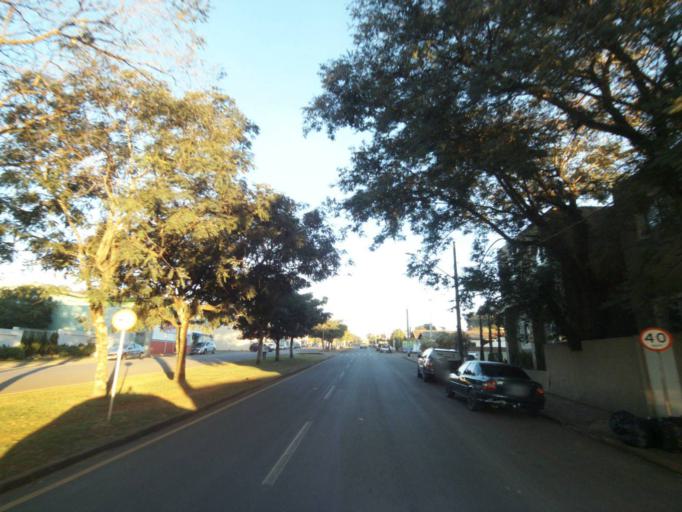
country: BR
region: Parana
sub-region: Tibagi
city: Tibagi
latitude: -24.5188
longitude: -50.4128
